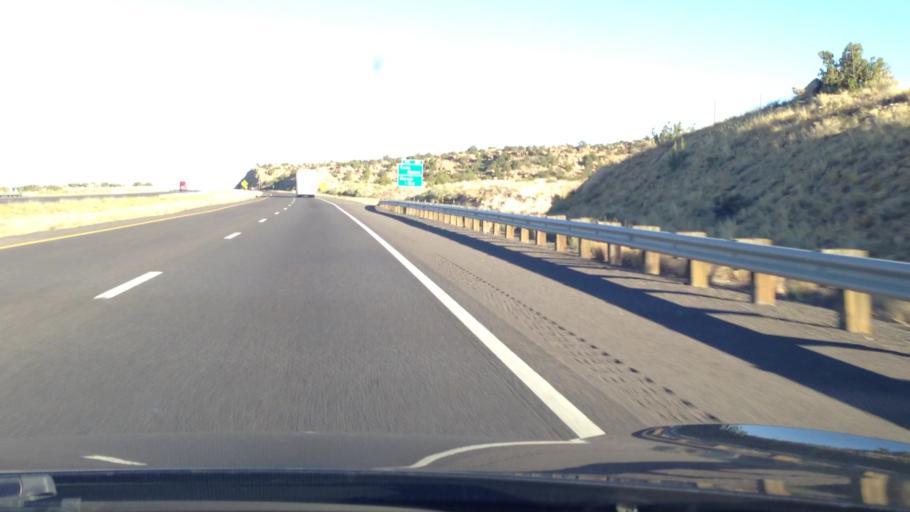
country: US
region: New Mexico
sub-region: Cibola County
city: Laguna
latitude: 35.0406
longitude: -107.4950
